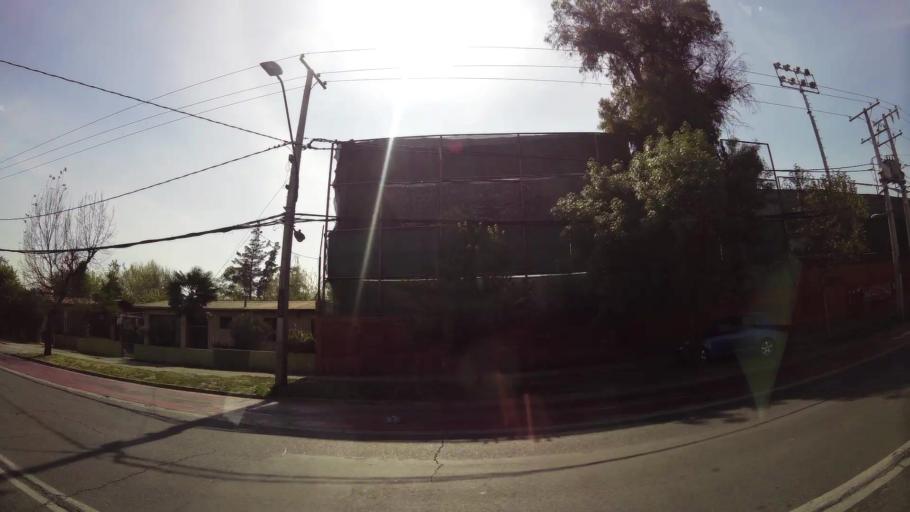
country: CL
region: Santiago Metropolitan
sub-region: Provincia de Santiago
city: Villa Presidente Frei, Nunoa, Santiago, Chile
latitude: -33.5000
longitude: -70.5957
